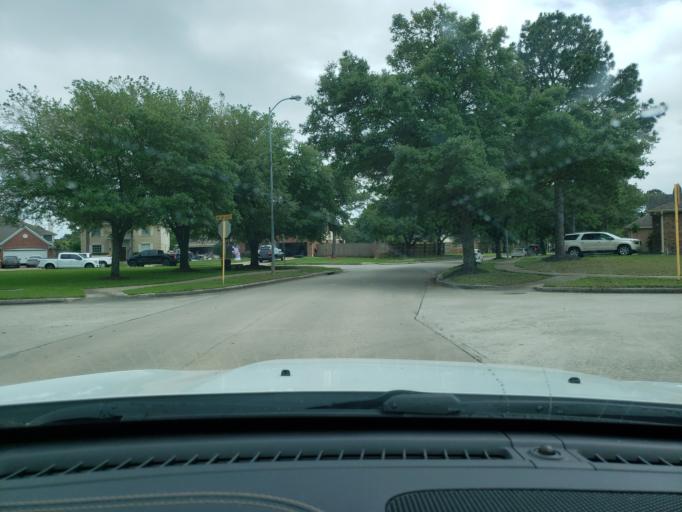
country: US
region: Texas
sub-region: Harris County
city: Jersey Village
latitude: 29.9224
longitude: -95.5661
